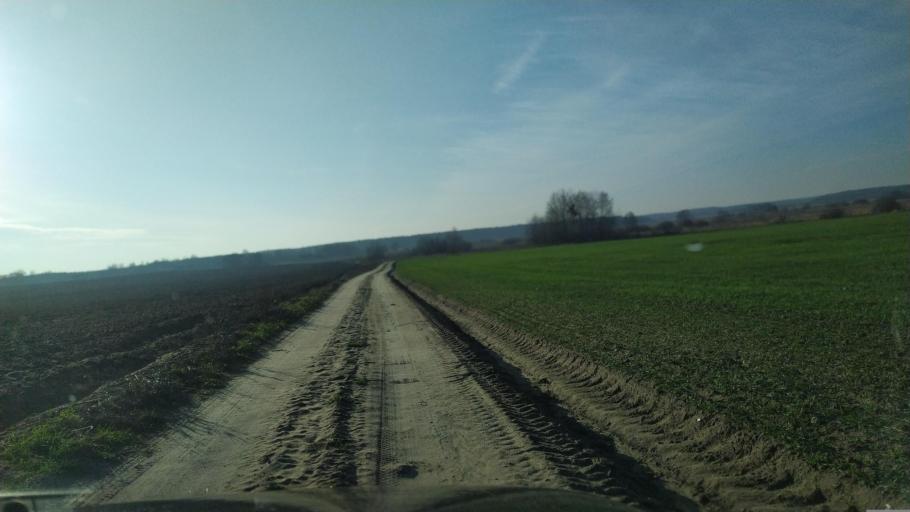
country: BY
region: Brest
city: Kamyanyets
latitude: 52.3802
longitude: 23.7798
